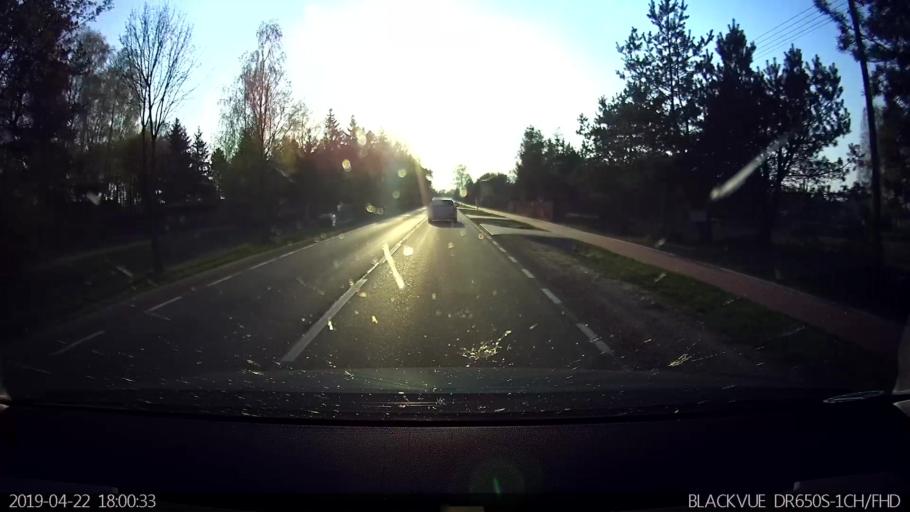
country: PL
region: Masovian Voivodeship
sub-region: Powiat wegrowski
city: Korytnica
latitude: 52.4763
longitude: 21.8447
